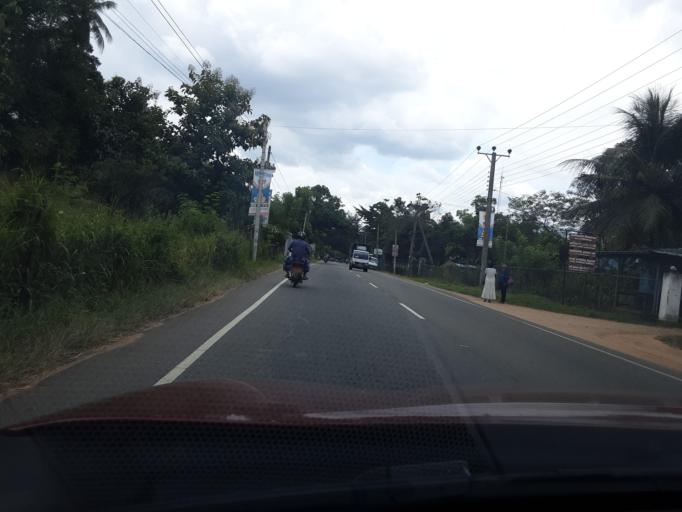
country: LK
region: North Western
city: Kurunegala
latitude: 7.4419
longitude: 80.2056
